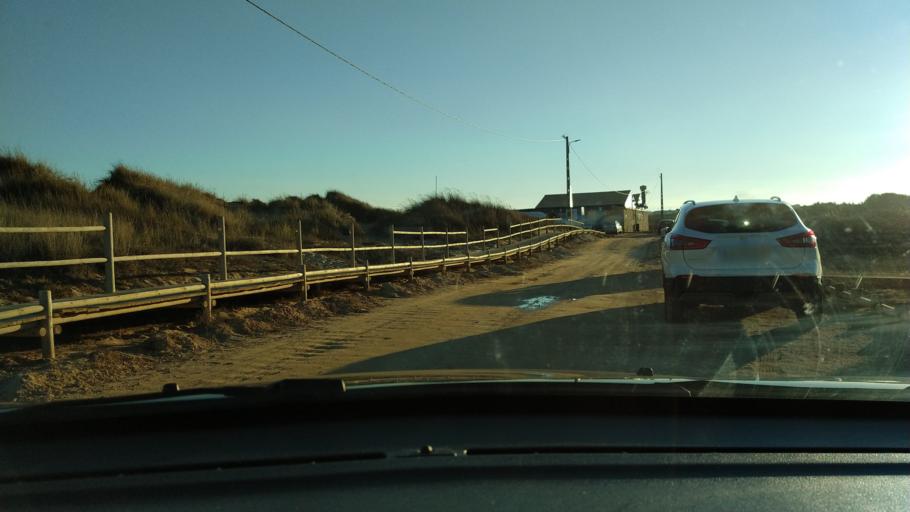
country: PT
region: Faro
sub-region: Vila do Bispo
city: Sagres
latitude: 37.0201
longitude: -8.9262
